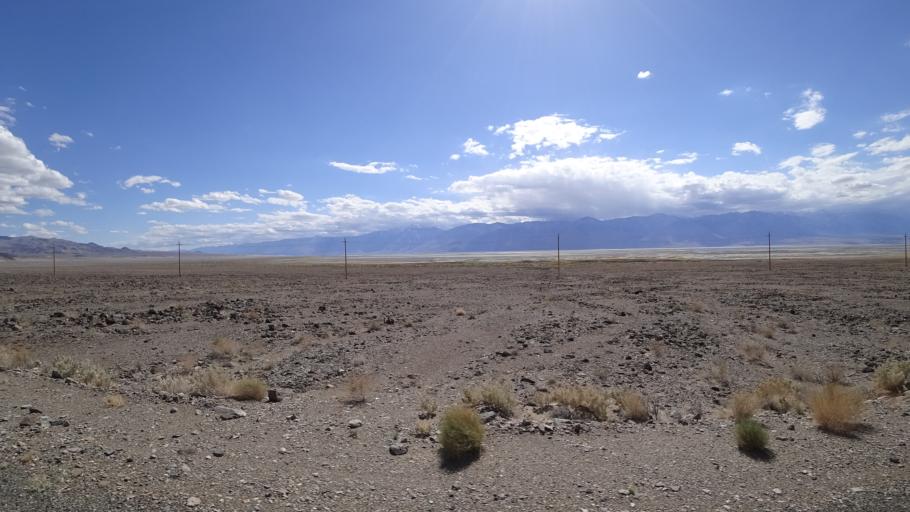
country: US
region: California
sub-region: Inyo County
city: Lone Pine
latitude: 36.4475
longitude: -117.8368
